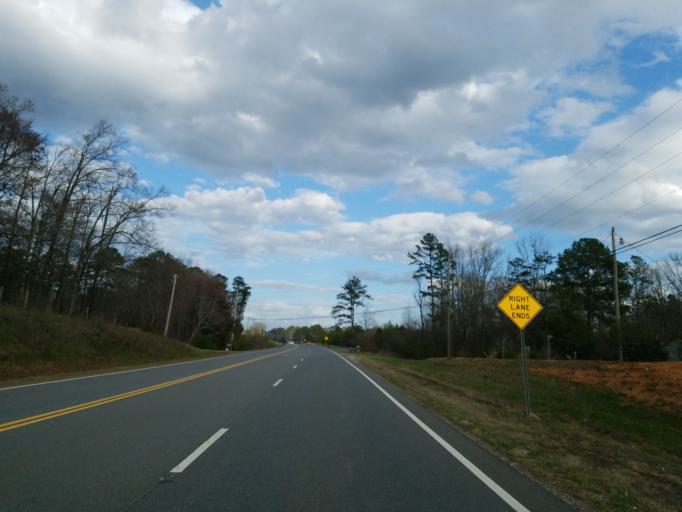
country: US
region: Georgia
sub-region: Bartow County
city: Rydal
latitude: 34.4479
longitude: -84.7796
